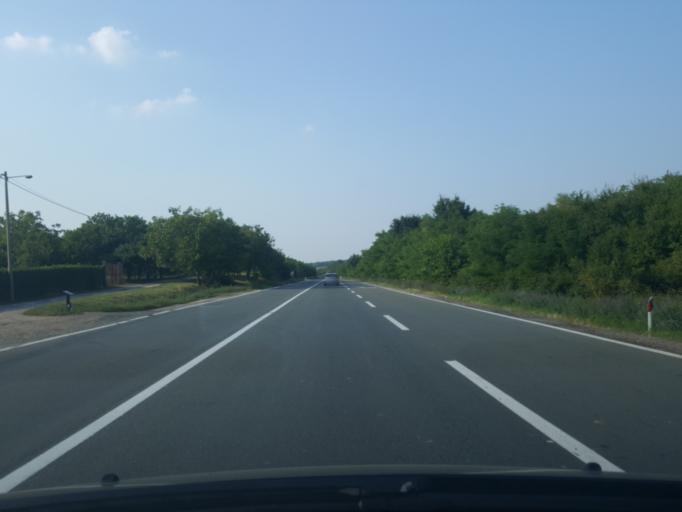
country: RS
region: Central Serbia
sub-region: Belgrade
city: Sopot
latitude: 44.5198
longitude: 20.6534
